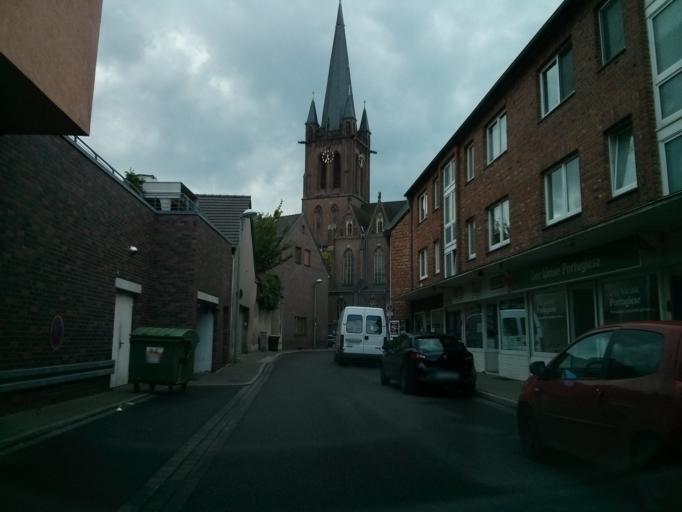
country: DE
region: North Rhine-Westphalia
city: Tonisvorst
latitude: 51.3726
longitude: 6.5113
